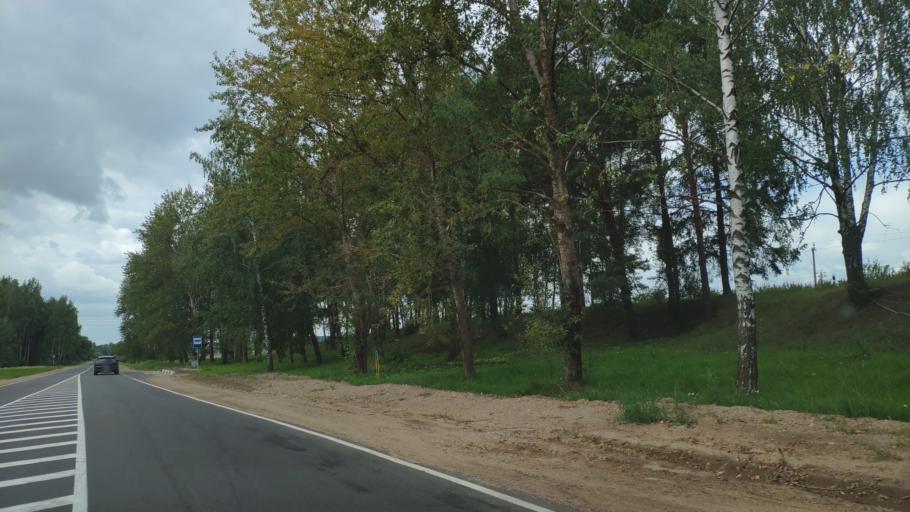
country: BY
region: Minsk
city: Syomkava
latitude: 53.9935
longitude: 27.4699
